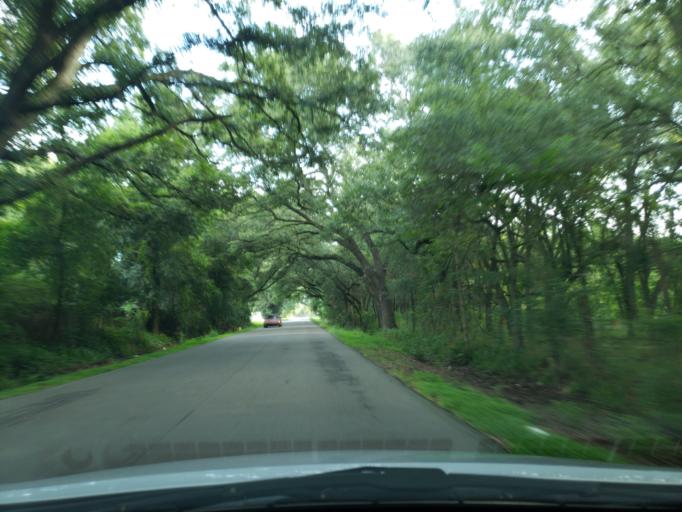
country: US
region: Florida
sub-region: Hillsborough County
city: Palm River-Clair Mel
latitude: 27.9285
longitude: -82.3606
